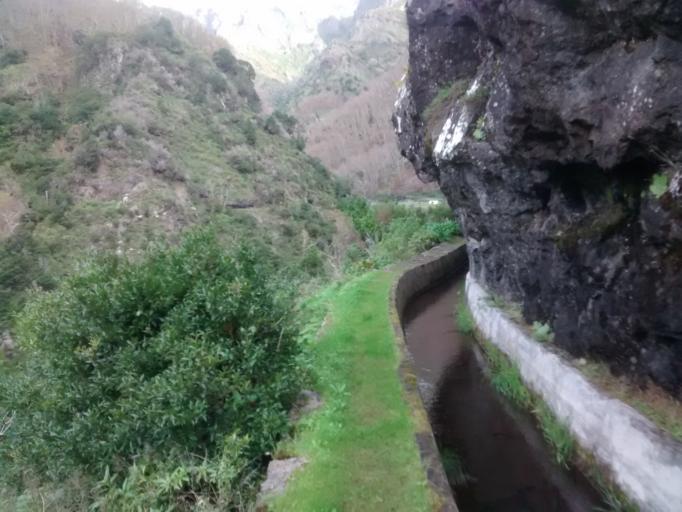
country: PT
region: Madeira
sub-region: Camara de Lobos
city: Curral das Freiras
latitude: 32.7277
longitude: -17.0110
